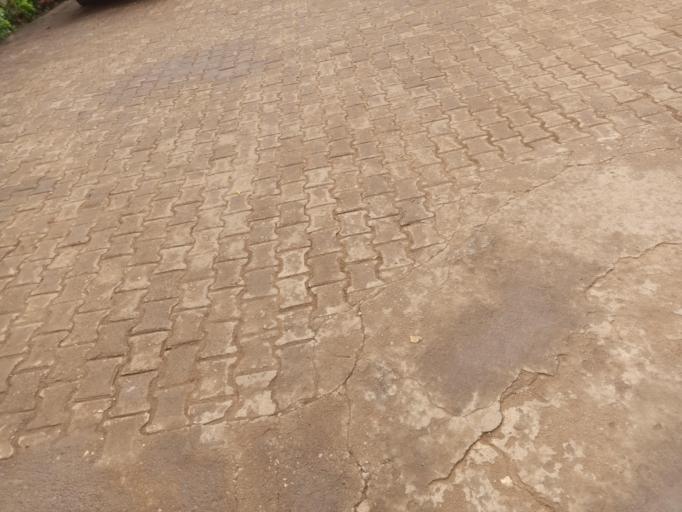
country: ML
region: Bamako
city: Bamako
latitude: 12.6608
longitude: -7.9984
